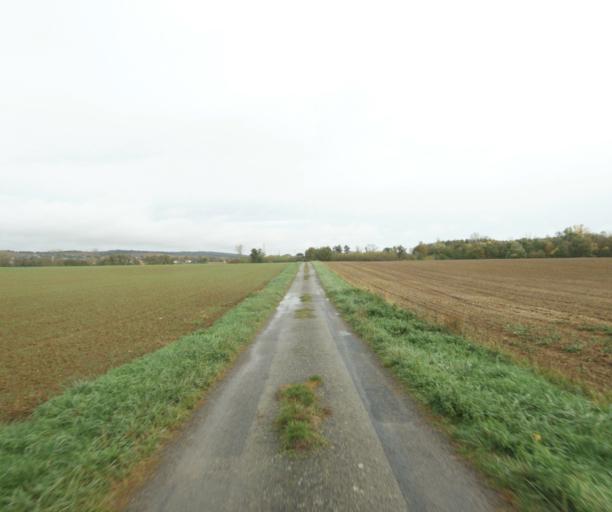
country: FR
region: Rhone-Alpes
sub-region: Departement de l'Ain
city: Pont-de-Vaux
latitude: 46.4854
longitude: 4.8892
